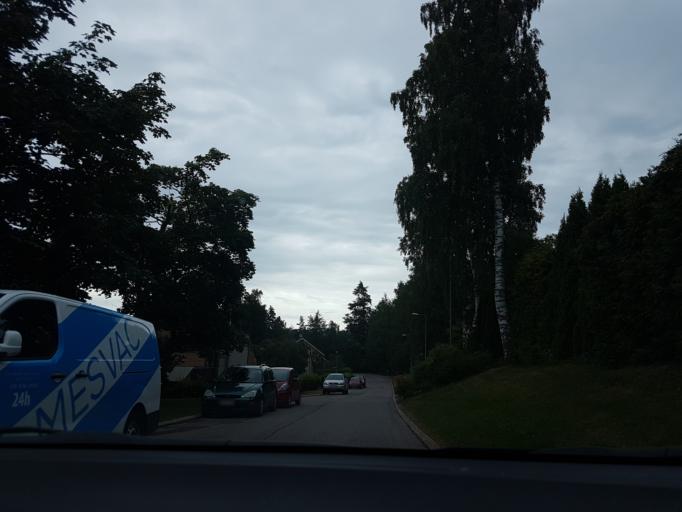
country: FI
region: Uusimaa
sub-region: Helsinki
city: Vantaa
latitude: 60.2197
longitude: 25.1275
